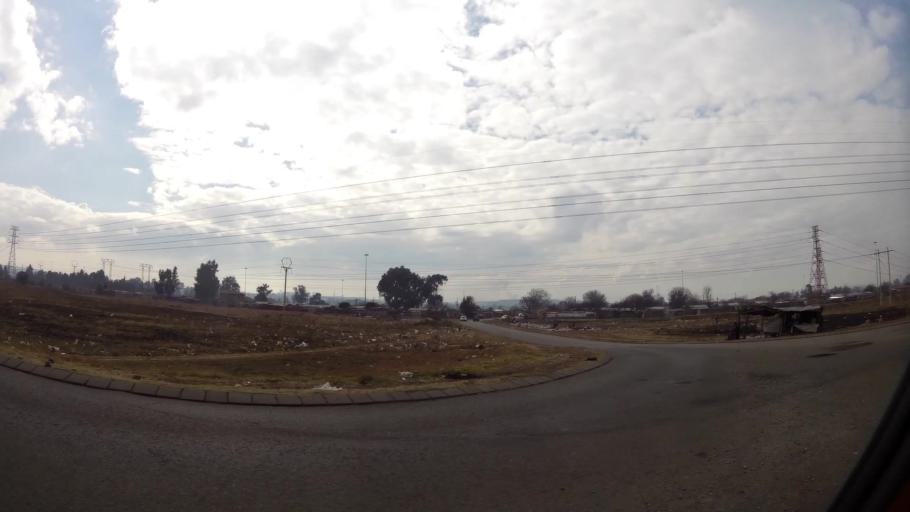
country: ZA
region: Gauteng
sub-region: Sedibeng District Municipality
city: Vanderbijlpark
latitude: -26.6761
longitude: 27.8427
